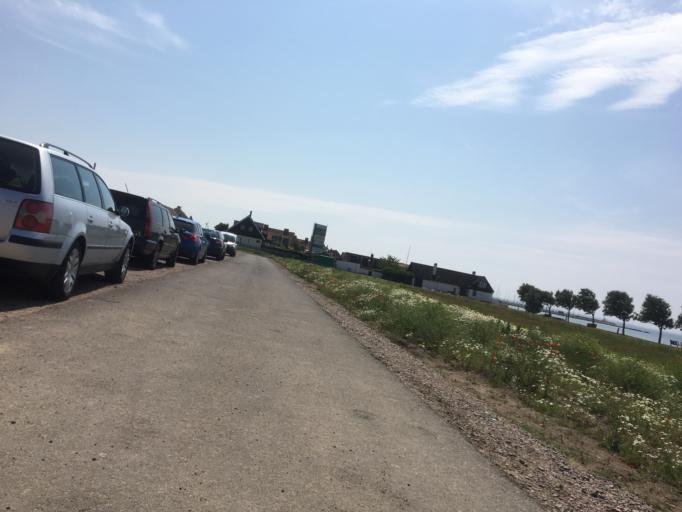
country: SE
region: Skane
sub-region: Landskrona
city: Landskrona
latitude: 55.9009
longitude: 12.8048
